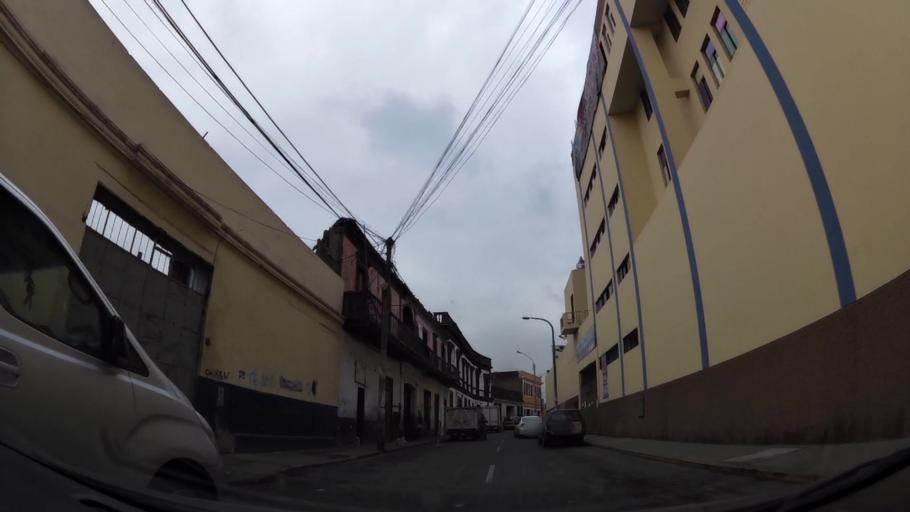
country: PE
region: Lima
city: Lima
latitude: -12.0417
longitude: -77.0365
